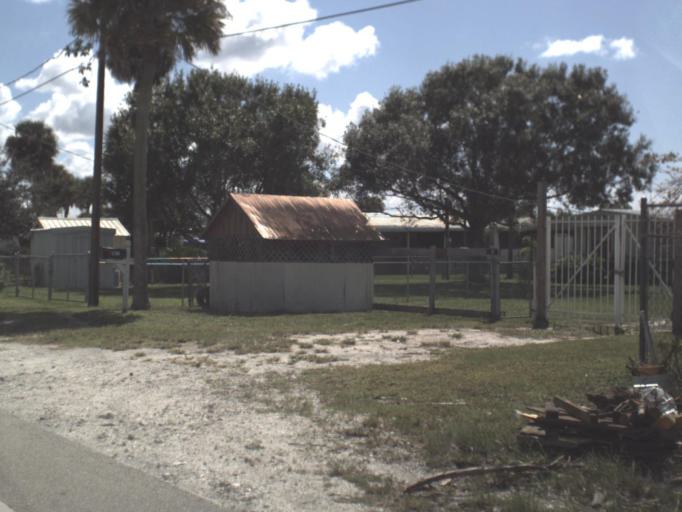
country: US
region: Florida
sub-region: Okeechobee County
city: Taylor Creek
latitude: 27.2020
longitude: -80.7758
